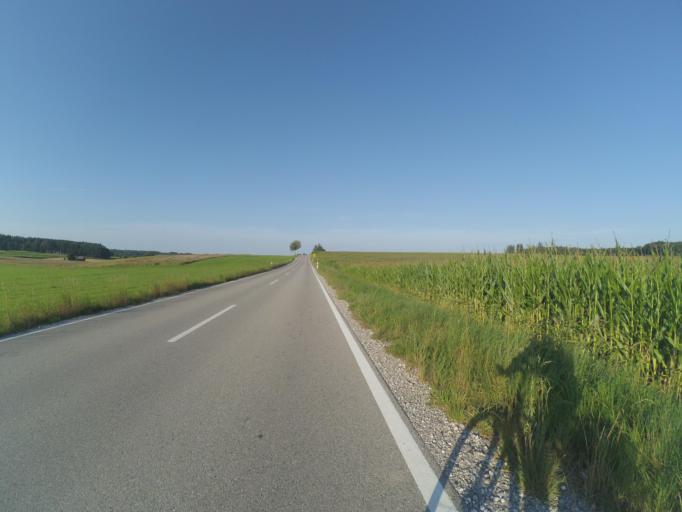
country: DE
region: Bavaria
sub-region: Swabia
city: Dirlewang
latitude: 48.0105
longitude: 10.5483
